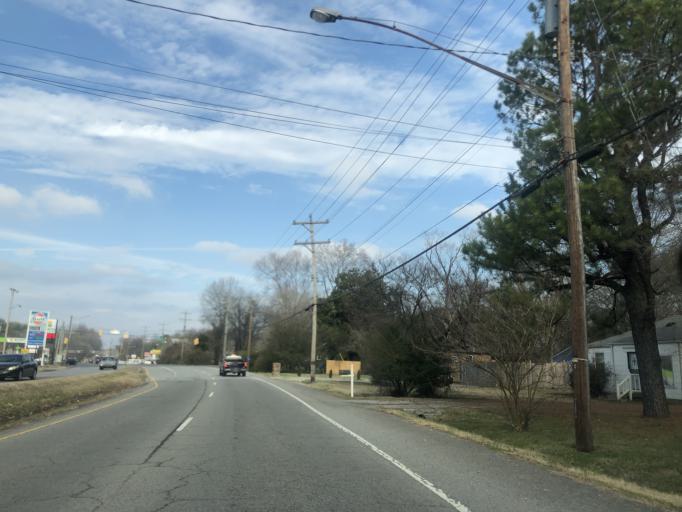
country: US
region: Tennessee
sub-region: Davidson County
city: Oak Hill
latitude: 36.1137
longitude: -86.7200
